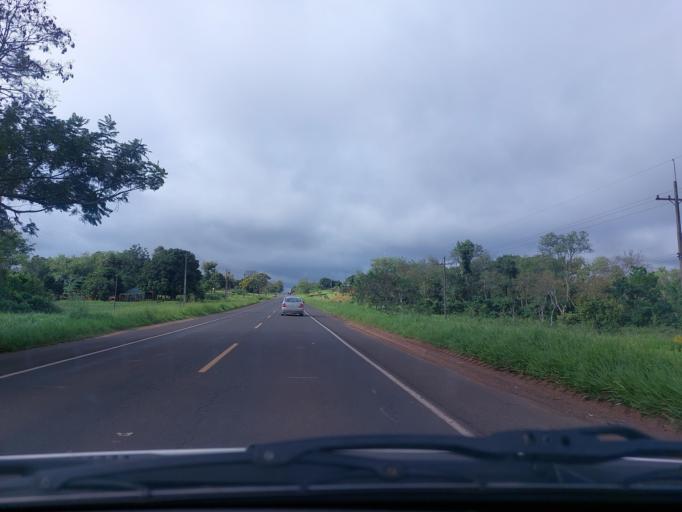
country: PY
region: San Pedro
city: Guayaybi
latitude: -24.5941
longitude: -56.3931
